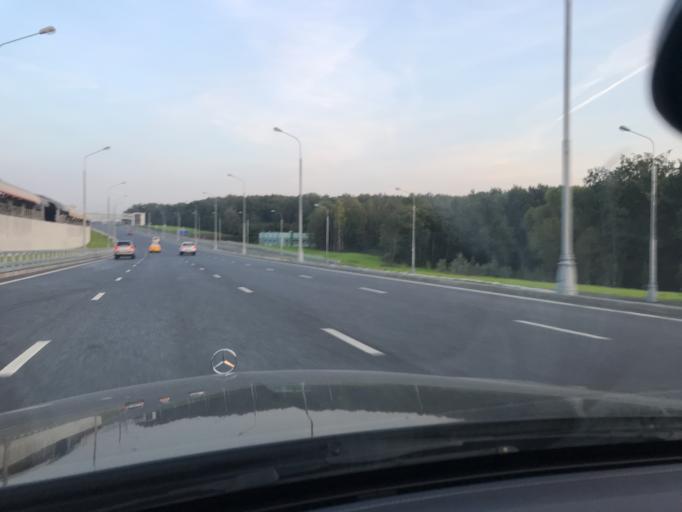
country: RU
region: Moskovskaya
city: Mosrentgen
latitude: 55.5892
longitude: 37.4261
